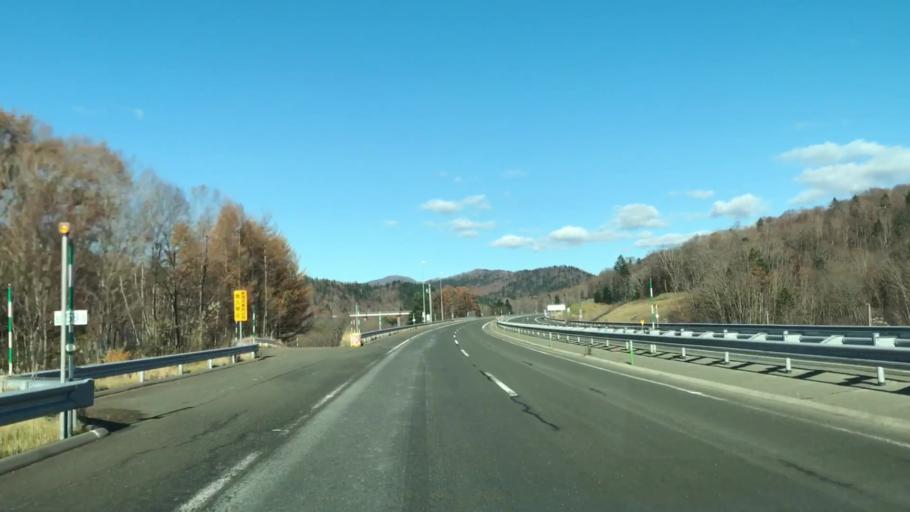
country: JP
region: Hokkaido
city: Shimo-furano
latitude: 42.9330
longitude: 142.2053
